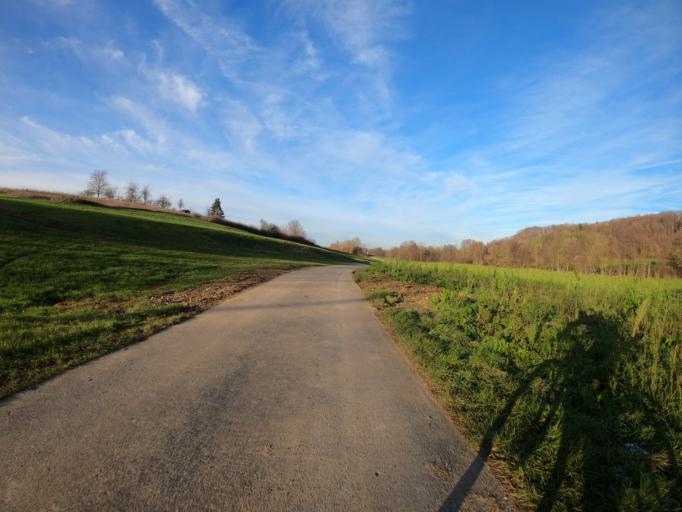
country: DE
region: Baden-Wuerttemberg
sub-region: Regierungsbezirk Stuttgart
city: Hattenhofen
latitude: 48.6586
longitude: 9.5798
